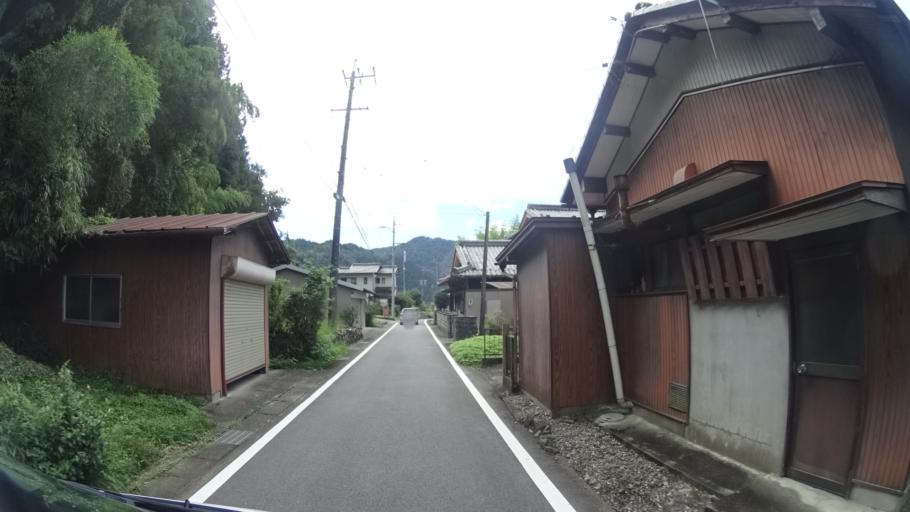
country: JP
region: Gifu
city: Minokamo
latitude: 35.5293
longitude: 137.1165
